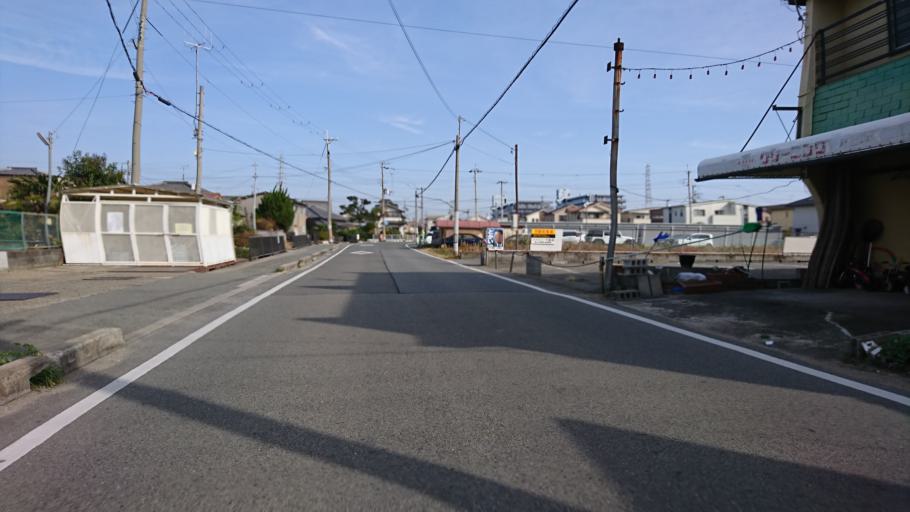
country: JP
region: Hyogo
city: Kakogawacho-honmachi
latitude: 34.7446
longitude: 134.8246
